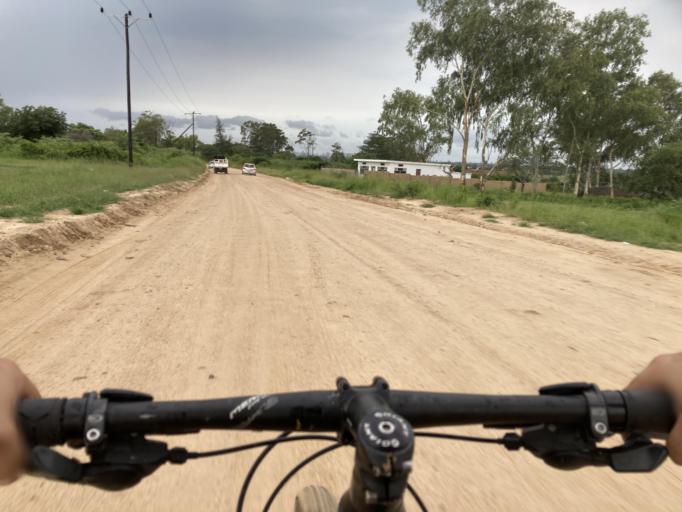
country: MZ
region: Maputo City
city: Maputo
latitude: -26.0342
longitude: 32.5427
